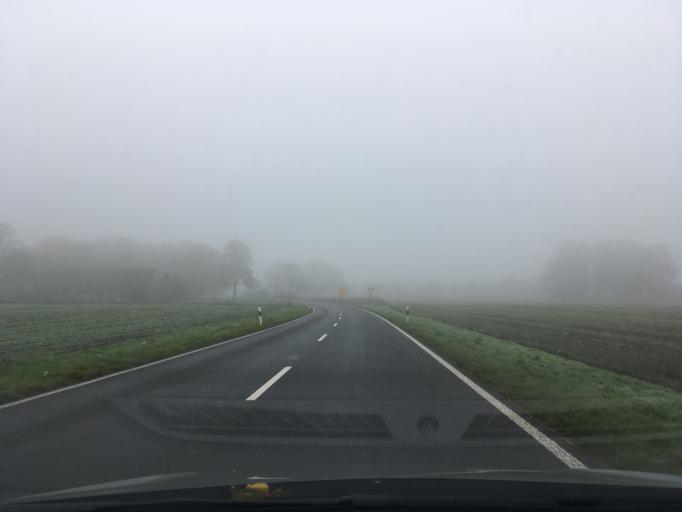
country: DE
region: North Rhine-Westphalia
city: Stadtlohn
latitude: 52.0607
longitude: 6.9372
